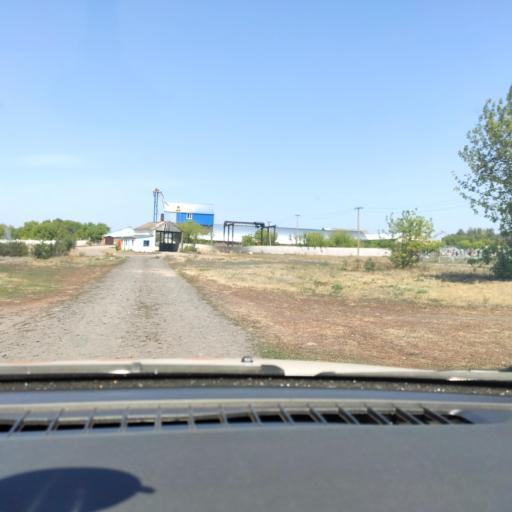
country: RU
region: Voronezj
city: Ol'khovatka
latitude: 50.5680
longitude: 39.2633
